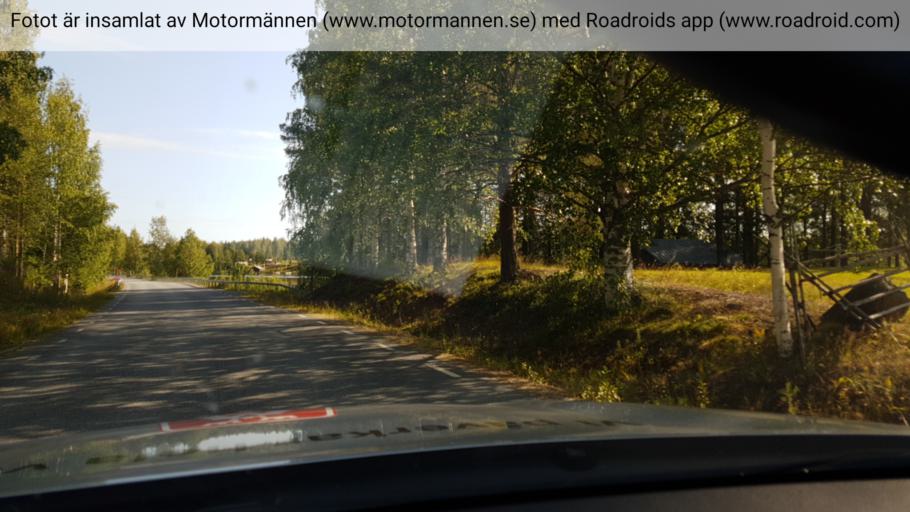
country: SE
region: Norrbotten
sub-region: Alvsbyns Kommun
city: AElvsbyn
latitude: 65.5838
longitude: 20.7049
